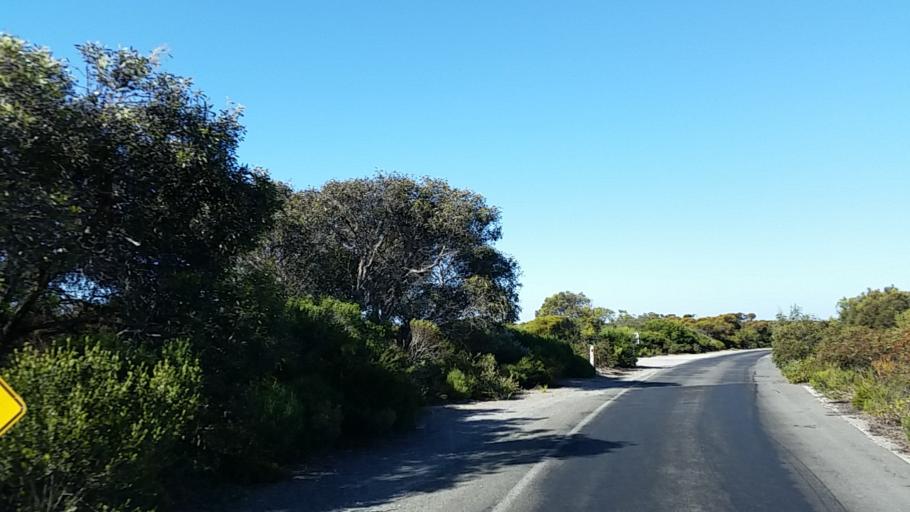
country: AU
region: South Australia
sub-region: Yorke Peninsula
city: Honiton
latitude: -35.2691
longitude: 136.9391
